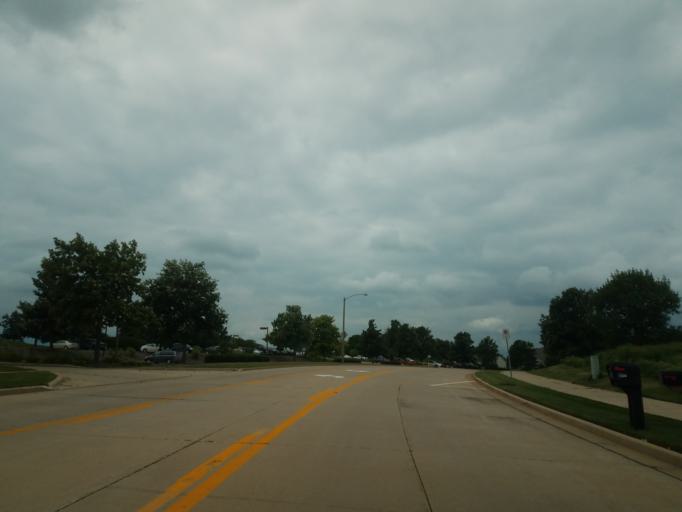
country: US
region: Illinois
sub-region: McLean County
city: Twin Grove
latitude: 40.4474
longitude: -89.0421
